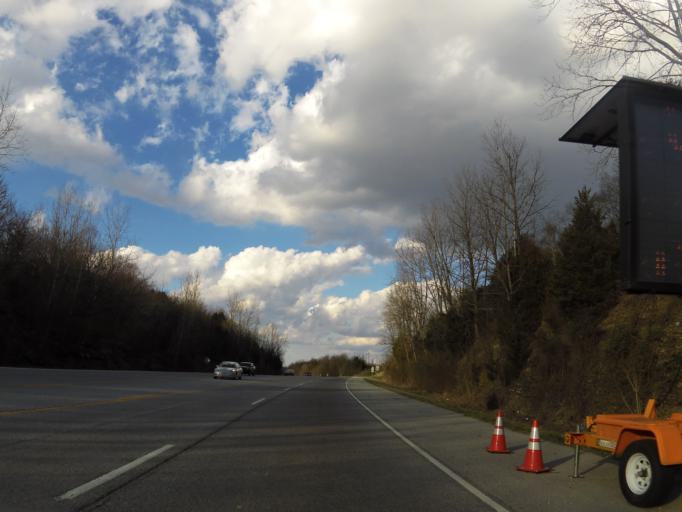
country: US
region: Tennessee
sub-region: Smith County
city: South Carthage
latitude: 36.2286
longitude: -85.9482
